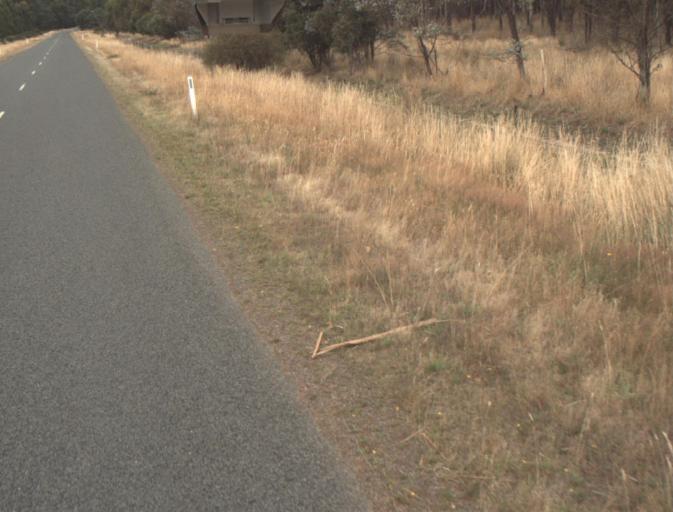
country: AU
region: Tasmania
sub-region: Northern Midlands
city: Evandale
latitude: -41.4850
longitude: 147.5035
